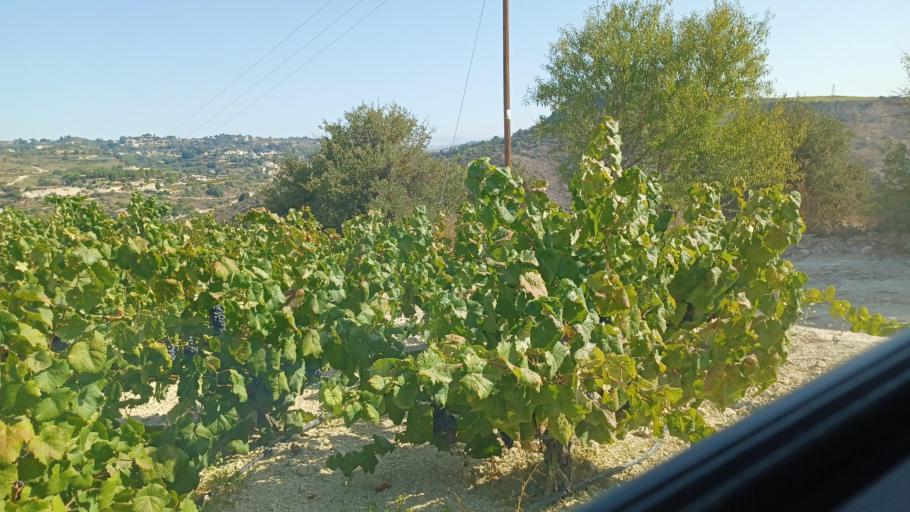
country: CY
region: Pafos
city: Tala
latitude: 34.8681
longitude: 32.4795
